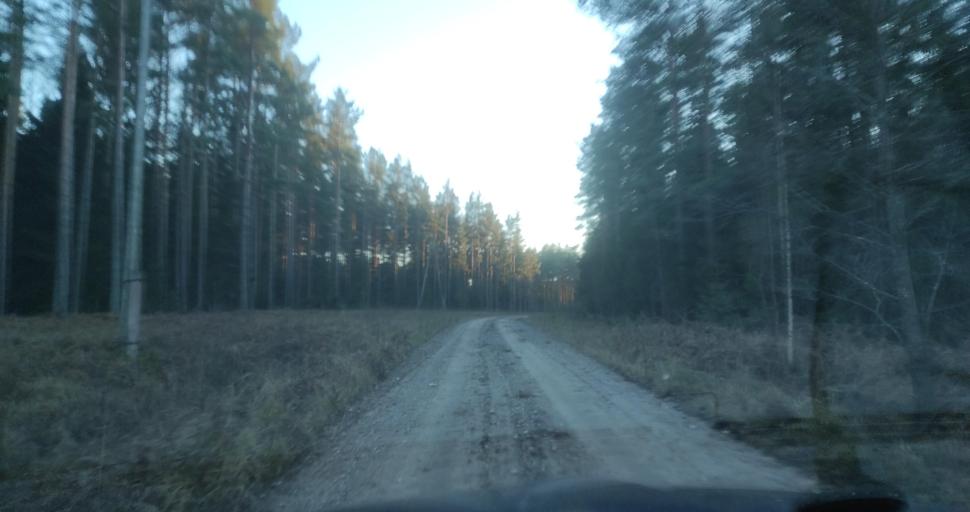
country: LV
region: Dundaga
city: Dundaga
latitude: 57.3741
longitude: 22.0785
